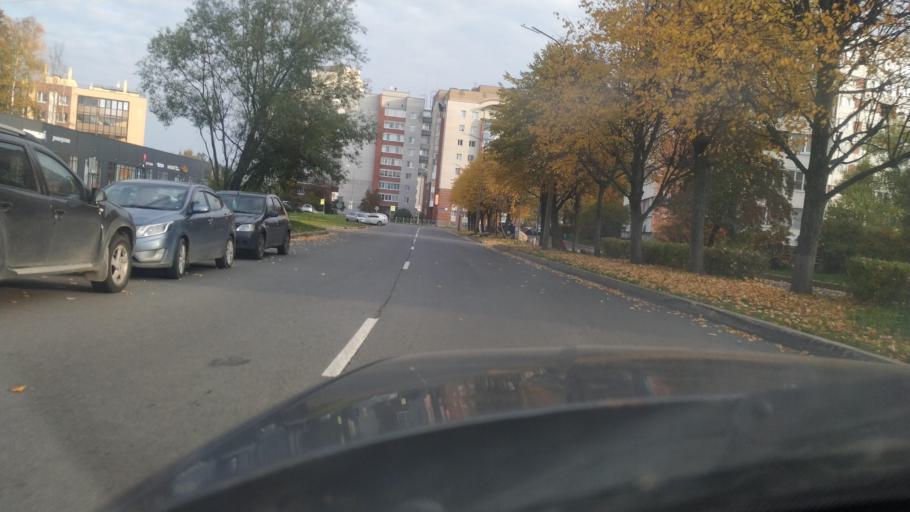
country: RU
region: Leningrad
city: Sosnovyy Bor
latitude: 59.9151
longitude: 29.0829
